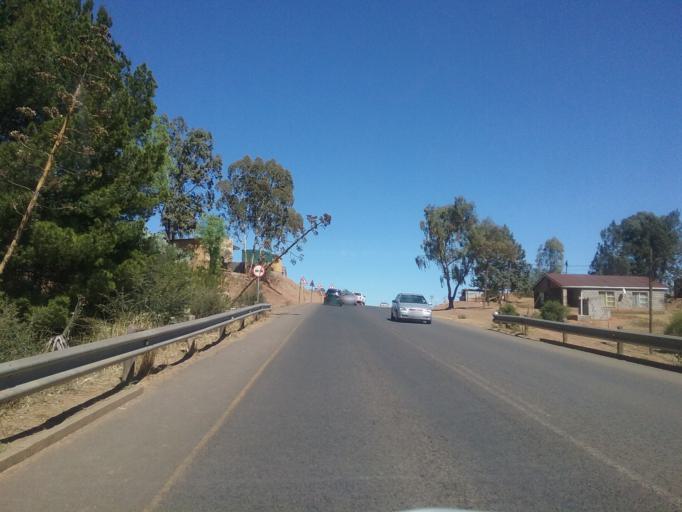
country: LS
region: Quthing
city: Quthing
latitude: -30.3982
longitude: 27.6670
